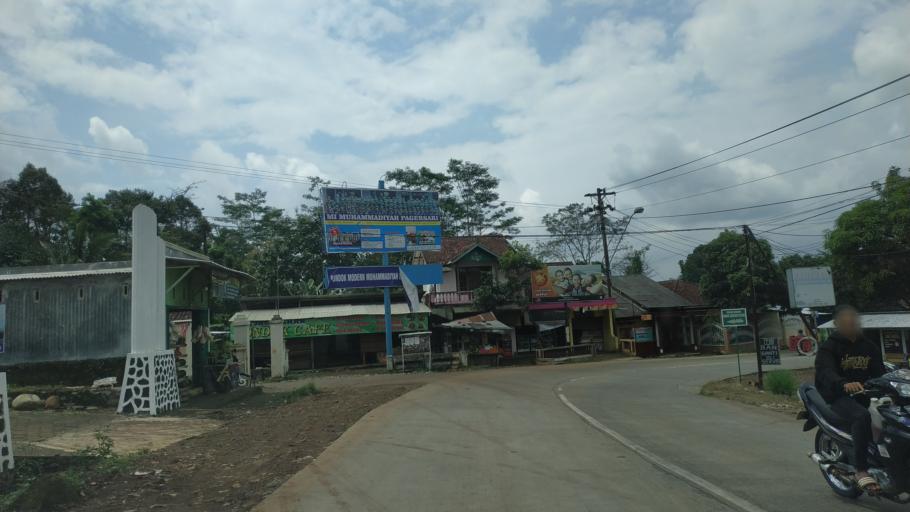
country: ID
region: Central Java
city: Weleri
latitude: -7.1059
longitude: 110.0770
